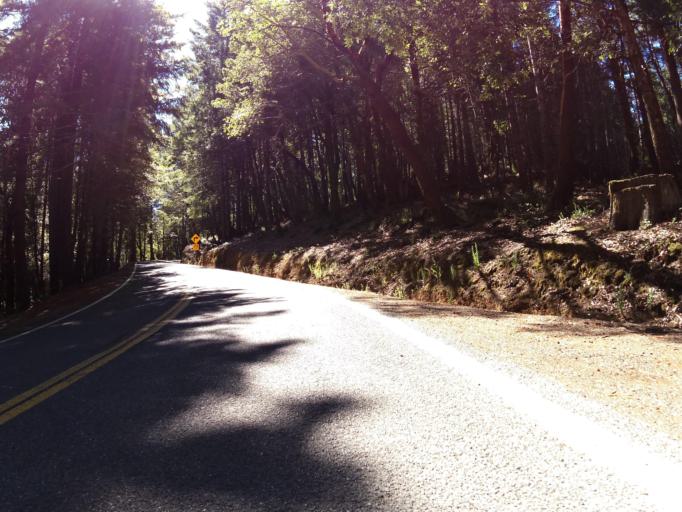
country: US
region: California
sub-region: Humboldt County
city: Redway
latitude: 39.8337
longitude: -123.7751
